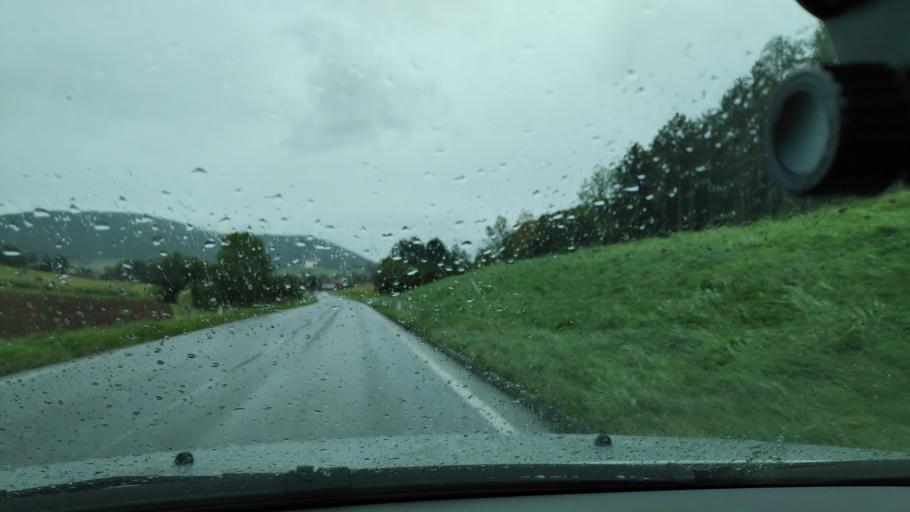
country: AT
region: Lower Austria
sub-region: Politischer Bezirk Neunkirchen
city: Schrattenbach
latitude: 47.7909
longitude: 16.0189
